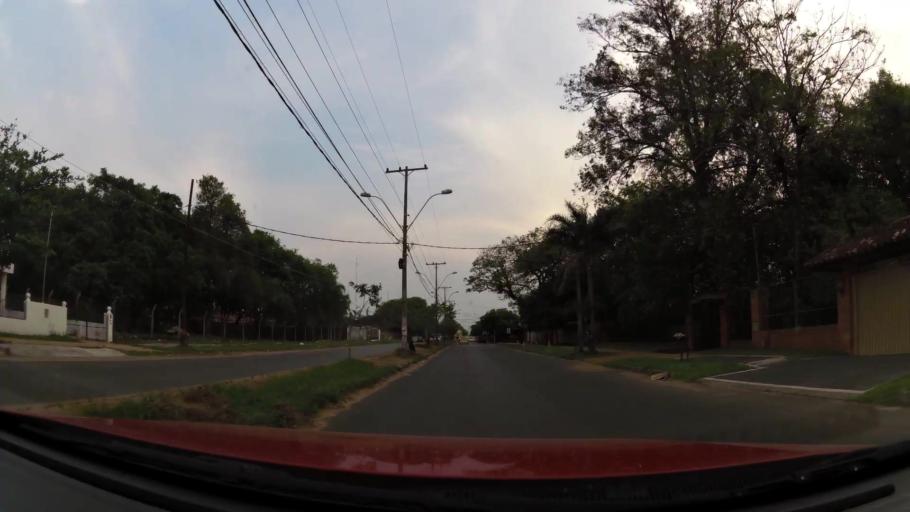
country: PY
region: Central
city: Lambare
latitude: -25.3582
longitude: -57.6447
